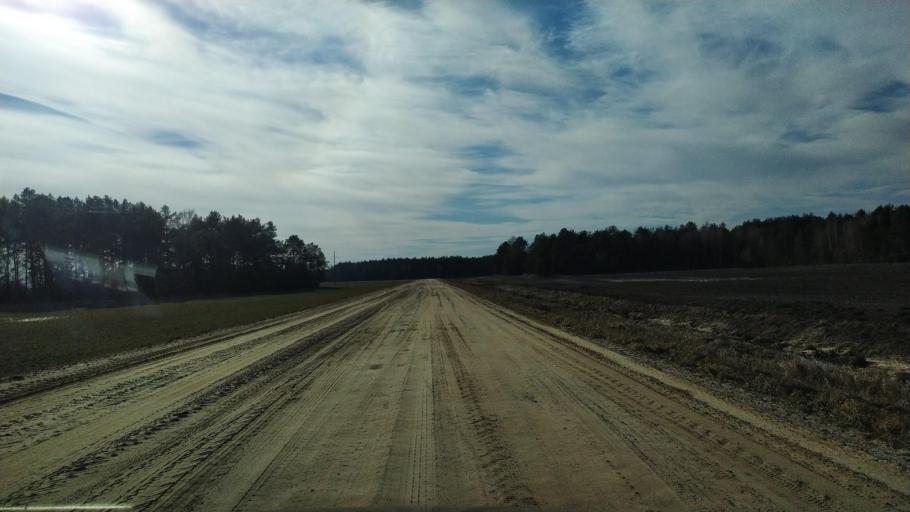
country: BY
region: Brest
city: Pruzhany
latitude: 52.5742
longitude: 24.3018
